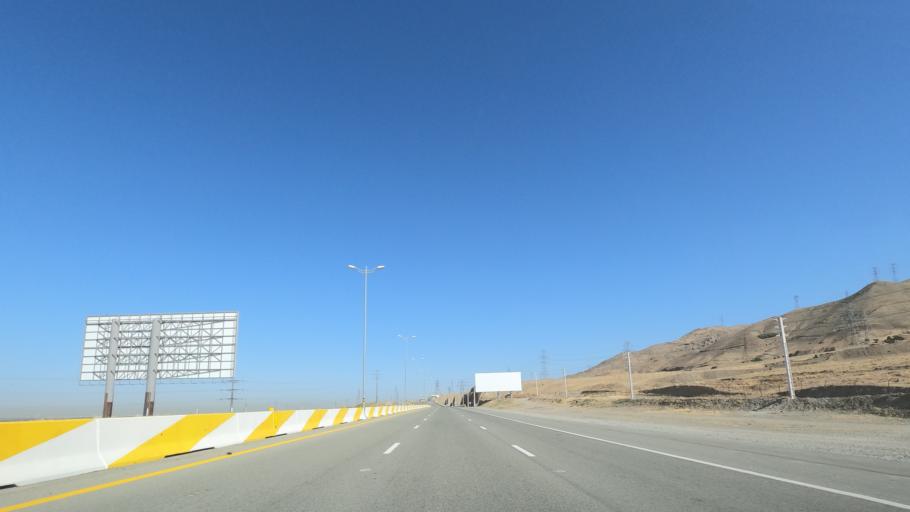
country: IR
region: Tehran
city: Shahr-e Qods
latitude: 35.7696
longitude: 51.0619
